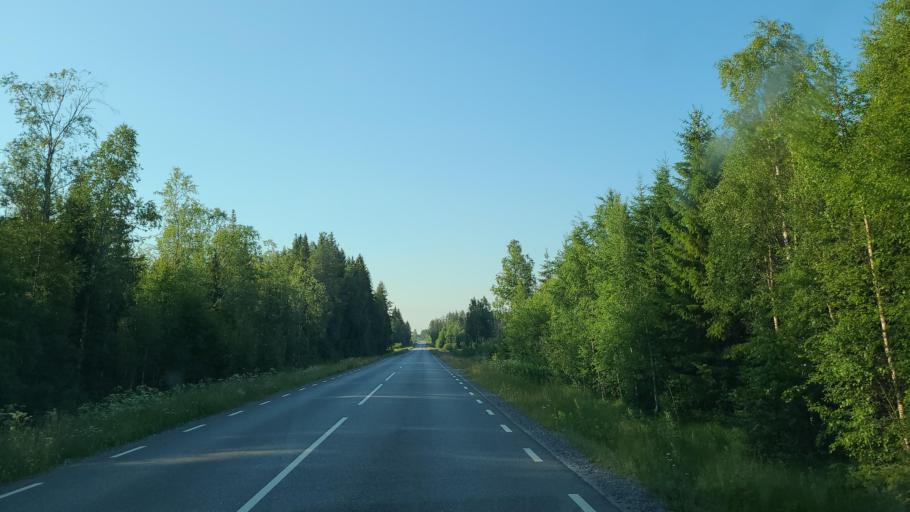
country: SE
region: Vaesterbotten
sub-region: Skelleftea Kommun
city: Burea
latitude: 64.4121
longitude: 21.3505
